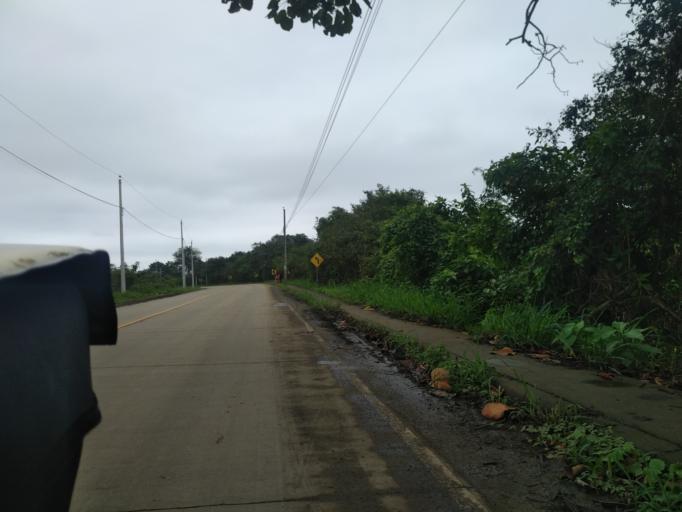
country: EC
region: Manabi
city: Jipijapa
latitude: -1.6733
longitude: -80.8100
